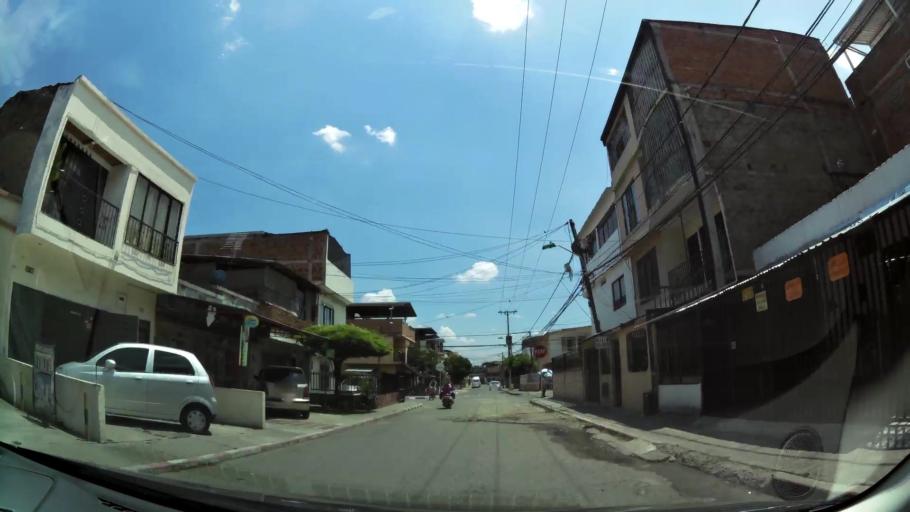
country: CO
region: Valle del Cauca
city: Cali
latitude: 3.4474
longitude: -76.5030
